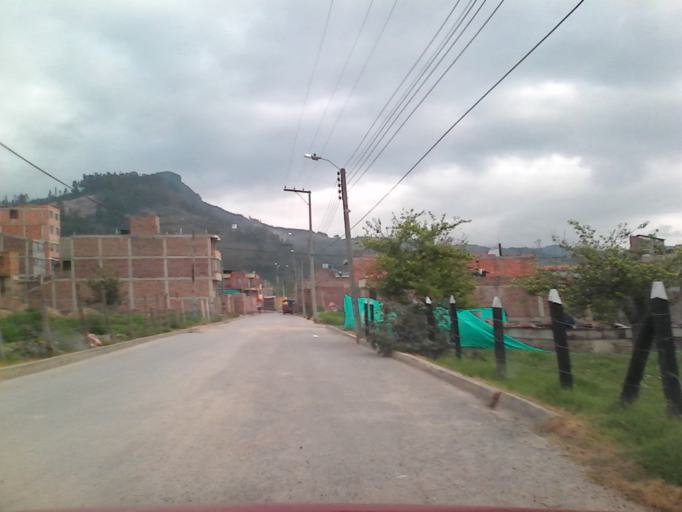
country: CO
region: Boyaca
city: Duitama
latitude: 5.8146
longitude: -73.0202
